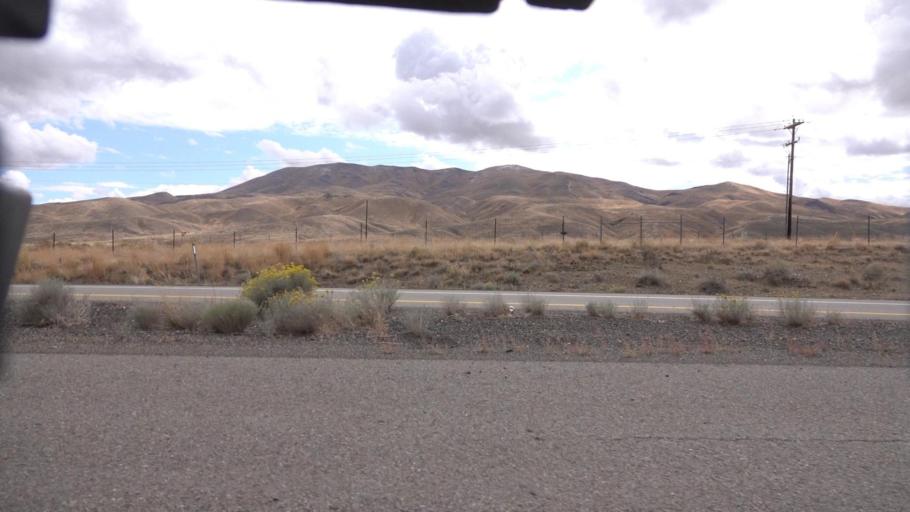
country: US
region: Nevada
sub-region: Elko County
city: Elko
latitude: 40.9321
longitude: -115.6679
